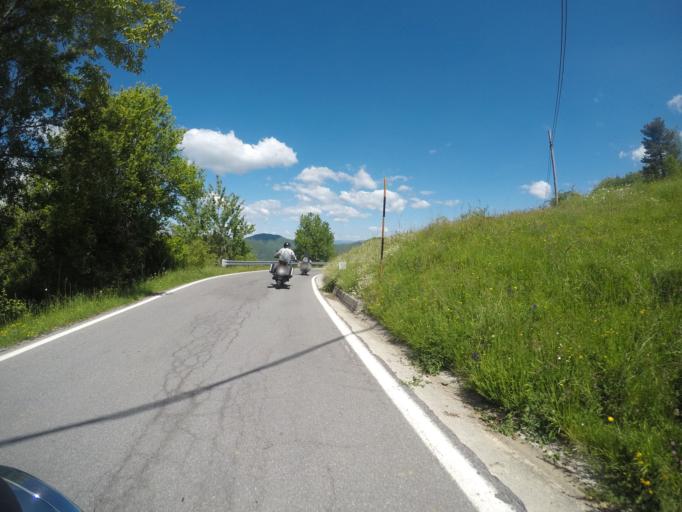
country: IT
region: Tuscany
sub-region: Provincia di Lucca
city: Careggine
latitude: 44.1059
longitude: 10.3332
